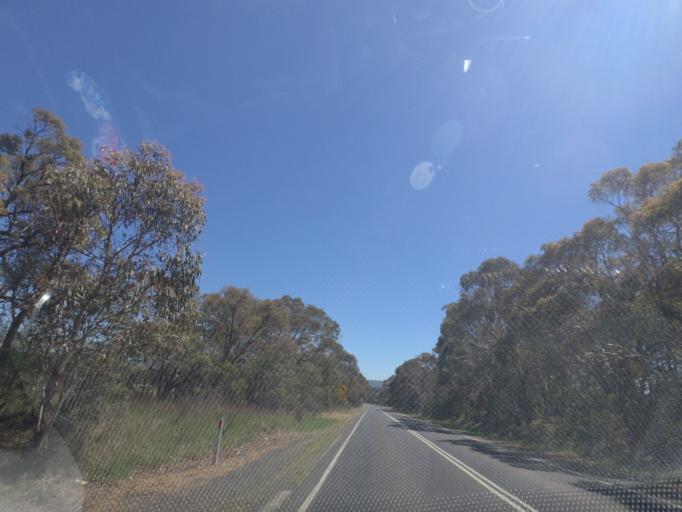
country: AU
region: Victoria
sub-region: Hume
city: Sunbury
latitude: -37.2892
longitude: 144.7888
